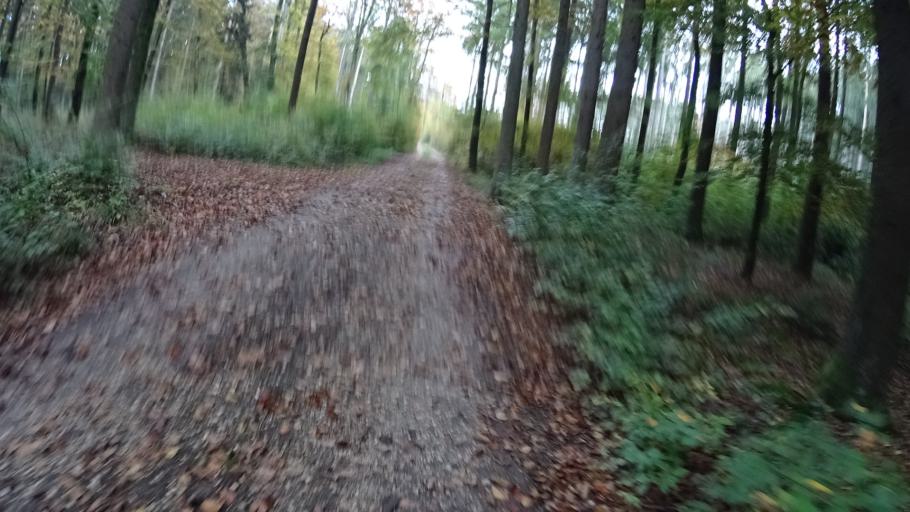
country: DE
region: Bavaria
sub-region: Upper Bavaria
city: Adelschlag
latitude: 48.8714
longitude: 11.2576
